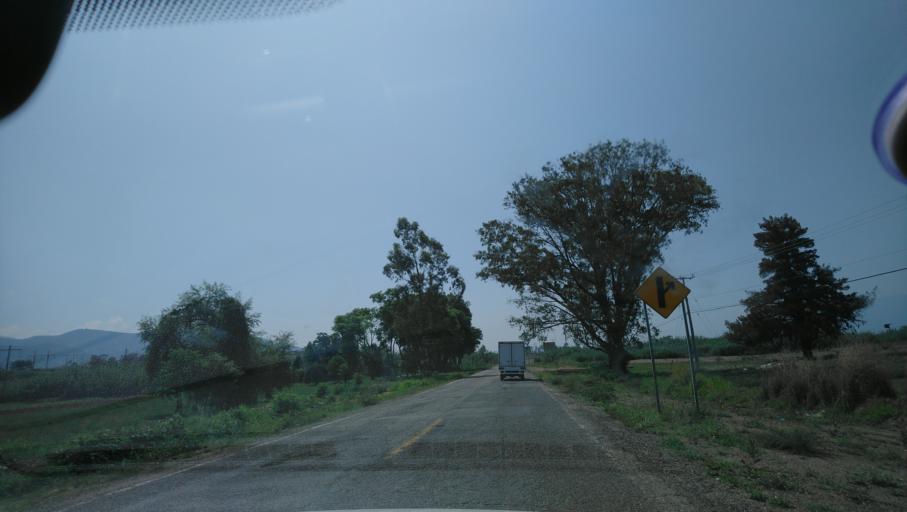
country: MX
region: Oaxaca
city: Santa Maria del Tule
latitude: 17.0402
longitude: -96.6227
